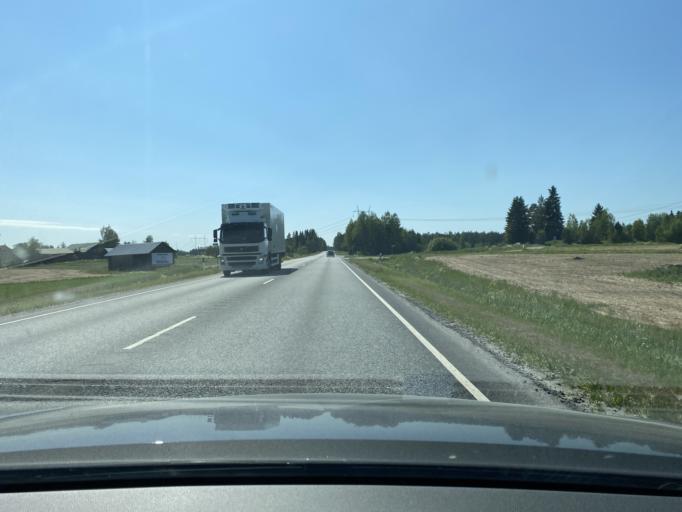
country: FI
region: Pirkanmaa
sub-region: Tampere
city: Nokia
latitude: 61.4172
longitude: 23.3214
